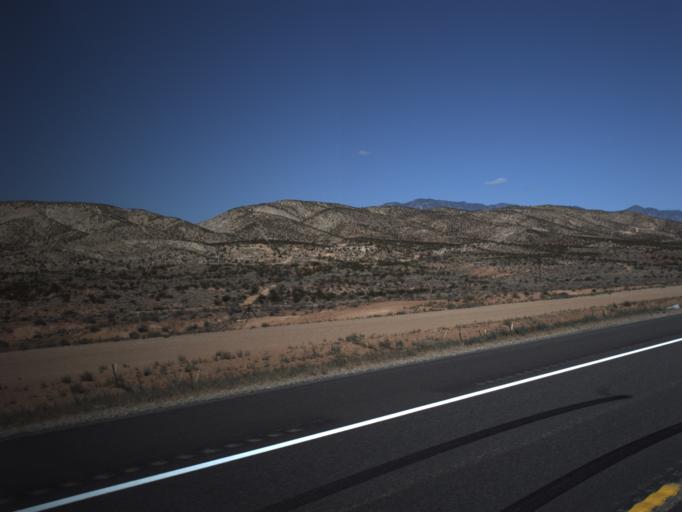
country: US
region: Utah
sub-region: Washington County
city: Washington
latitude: 37.0861
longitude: -113.4761
